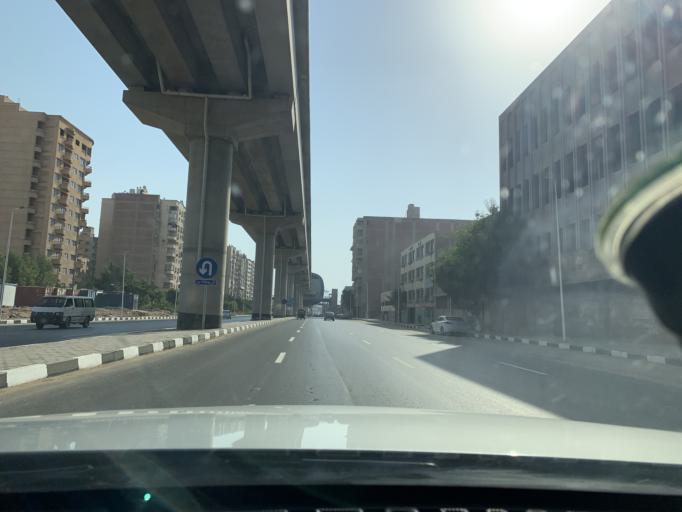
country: EG
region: Muhafazat al Qalyubiyah
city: Al Khankah
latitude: 30.1321
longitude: 31.3763
